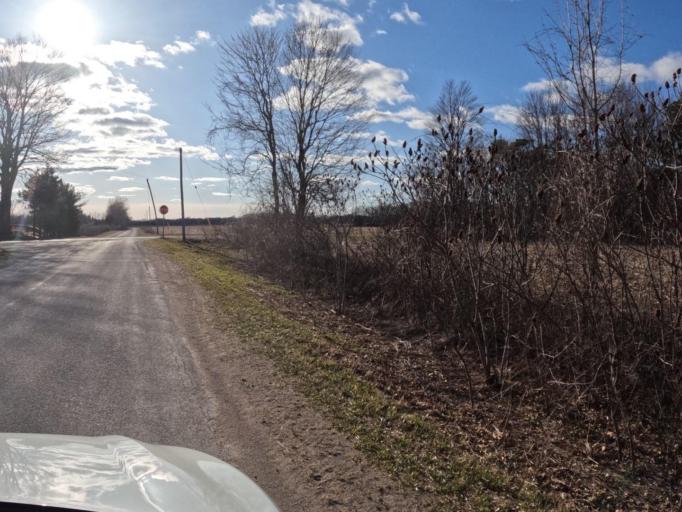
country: CA
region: Ontario
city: Norfolk County
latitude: 42.8154
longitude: -80.5647
